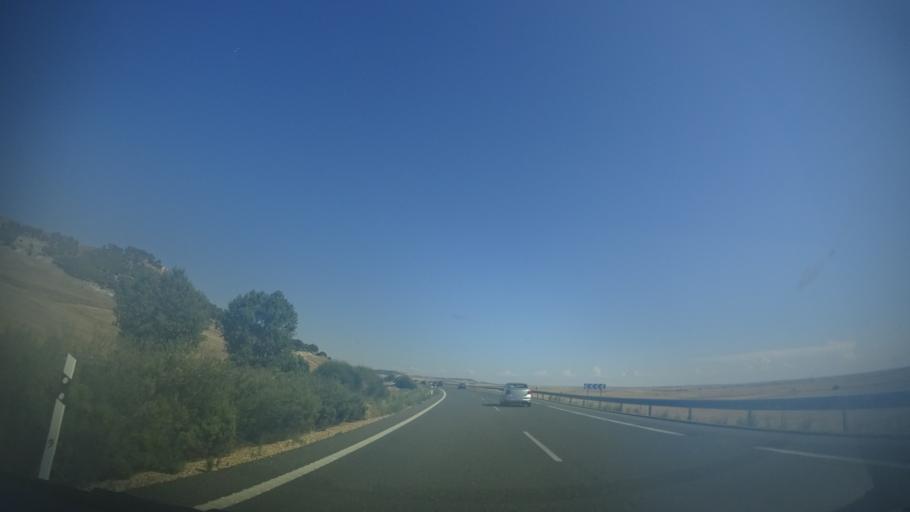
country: ES
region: Castille and Leon
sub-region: Provincia de Valladolid
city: Marzales
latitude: 41.6116
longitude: -5.1521
